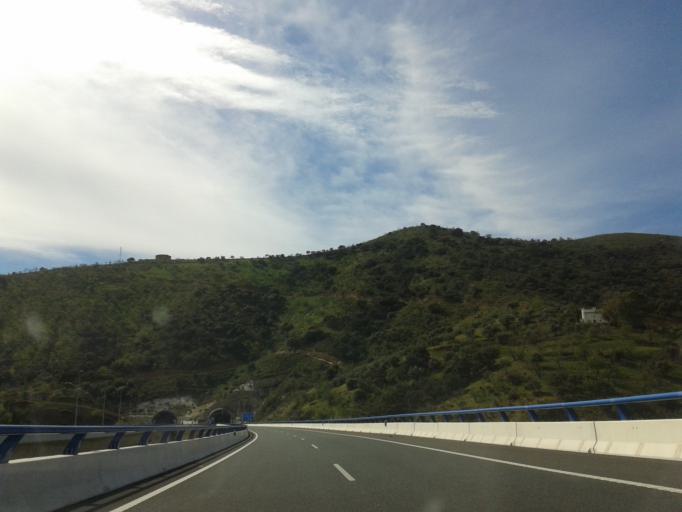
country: ES
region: Andalusia
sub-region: Provincia de Malaga
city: Casabermeja
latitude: 36.8738
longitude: -4.4829
